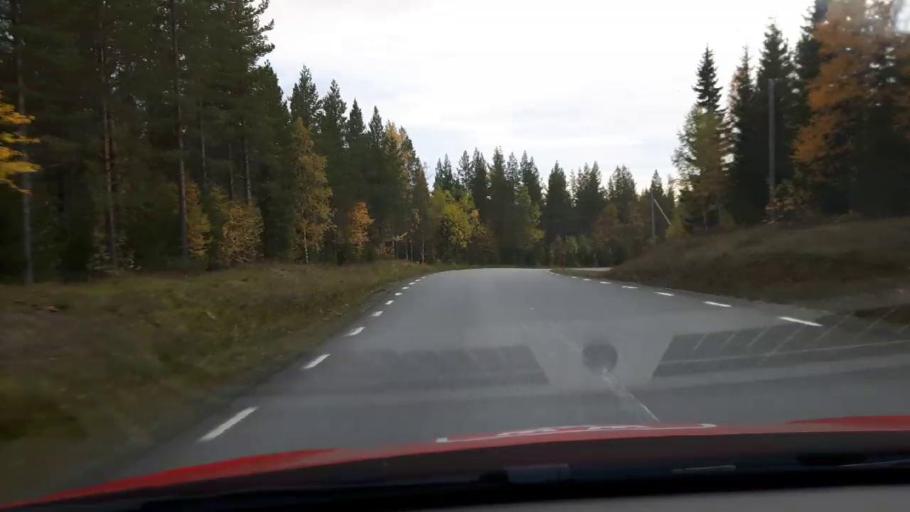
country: SE
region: Jaemtland
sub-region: OEstersunds Kommun
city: Lit
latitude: 63.3124
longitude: 15.1371
